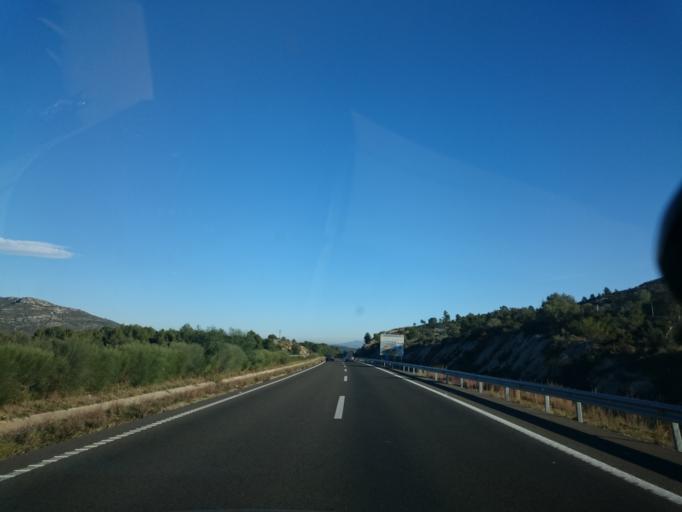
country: ES
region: Valencia
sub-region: Provincia de Castello
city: Santa Magdalena de Pulpis
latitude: 40.3806
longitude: 0.3415
